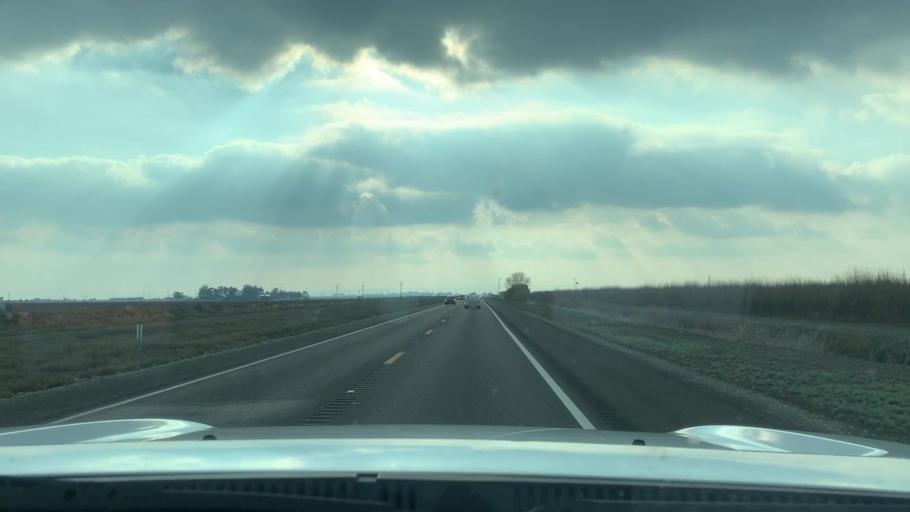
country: US
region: California
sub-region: Kings County
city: Stratford
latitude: 36.1644
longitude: -119.8477
